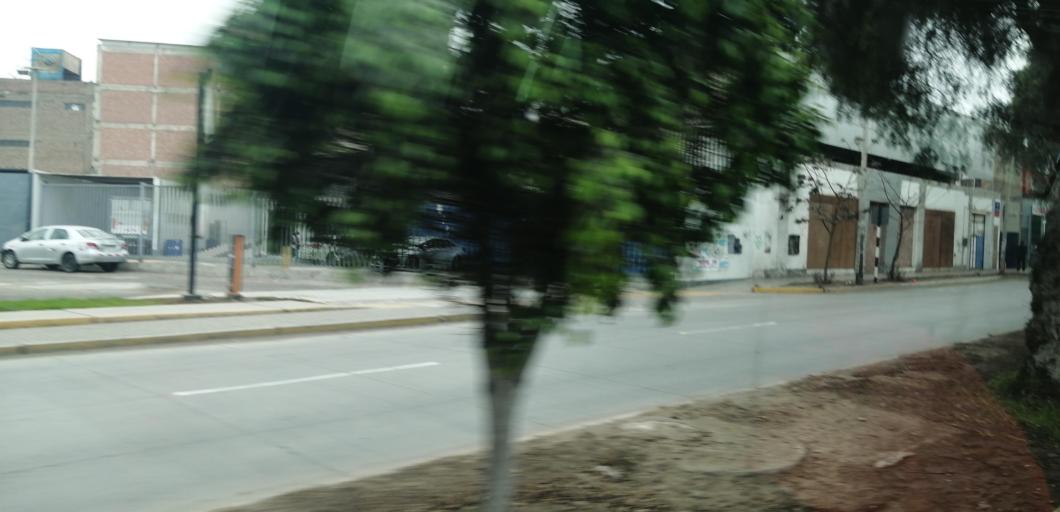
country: PE
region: La Libertad
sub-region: Provincia de Trujillo
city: Trujillo
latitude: -8.1047
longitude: -79.0339
